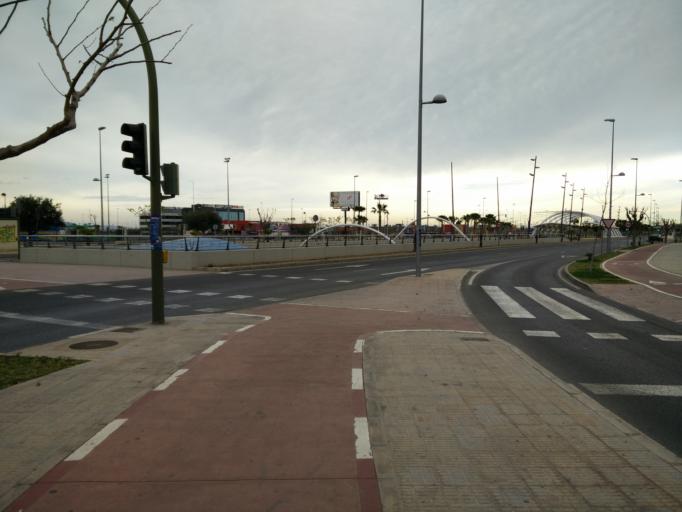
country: ES
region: Valencia
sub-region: Provincia de Castello
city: Castello de la Plana
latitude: 39.9835
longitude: -0.0246
